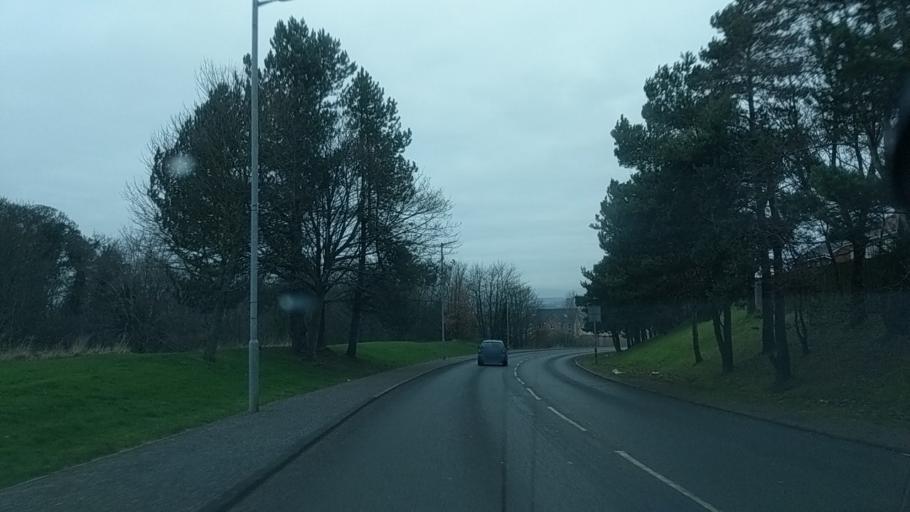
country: GB
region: Scotland
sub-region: South Lanarkshire
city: Rutherglen
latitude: 55.8101
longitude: -4.1844
